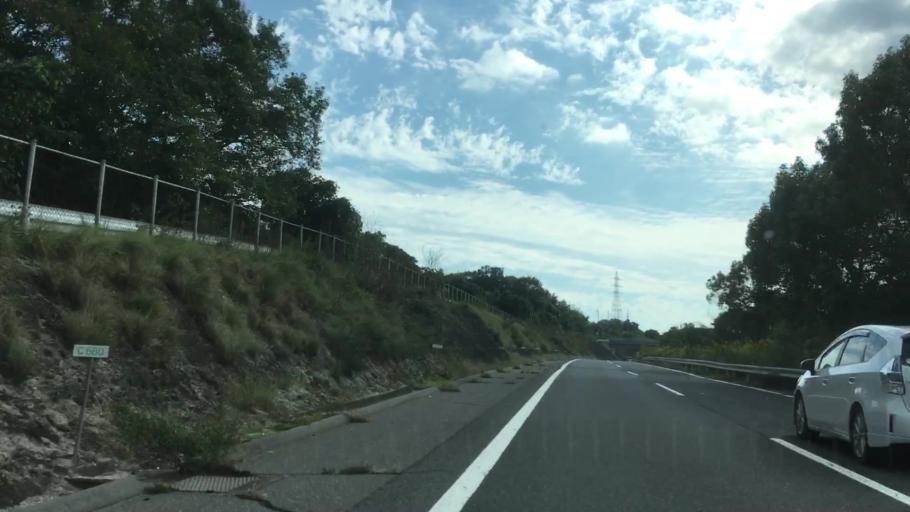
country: JP
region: Hiroshima
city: Hatsukaichi
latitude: 34.3339
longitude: 132.2947
